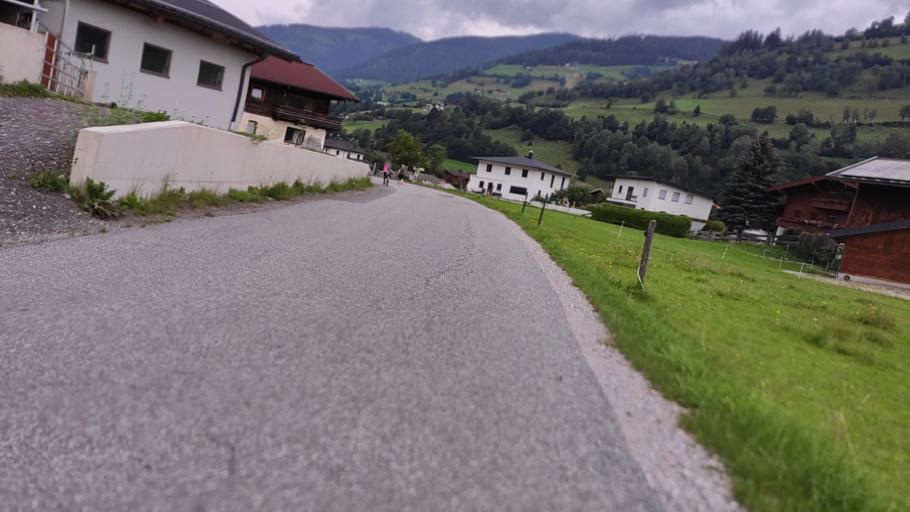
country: AT
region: Salzburg
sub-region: Politischer Bezirk Zell am See
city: Niedernsill
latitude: 47.2825
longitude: 12.6570
